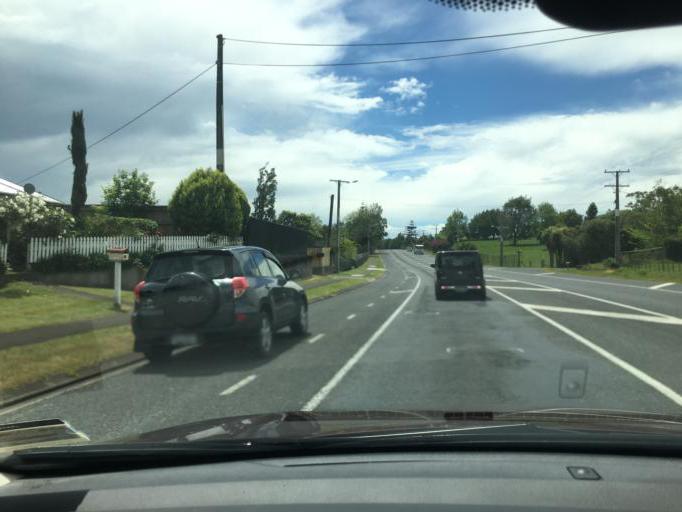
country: NZ
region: Waikato
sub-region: Waipa District
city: Cambridge
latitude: -37.9266
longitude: 175.3101
